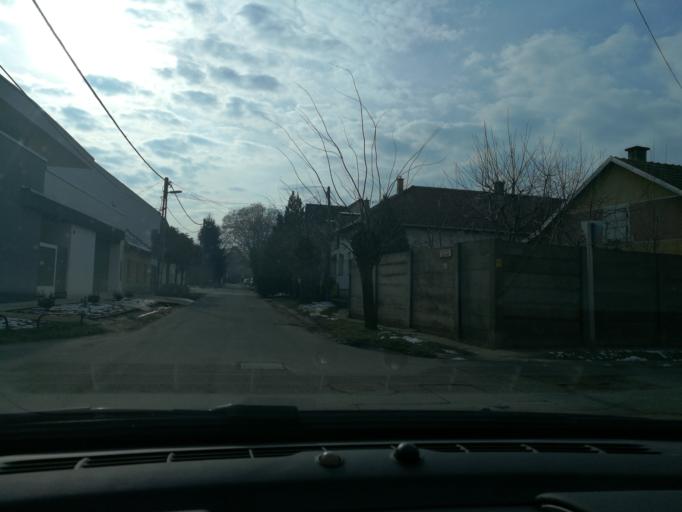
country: HU
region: Szabolcs-Szatmar-Bereg
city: Nyiregyhaza
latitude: 47.9477
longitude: 21.7222
